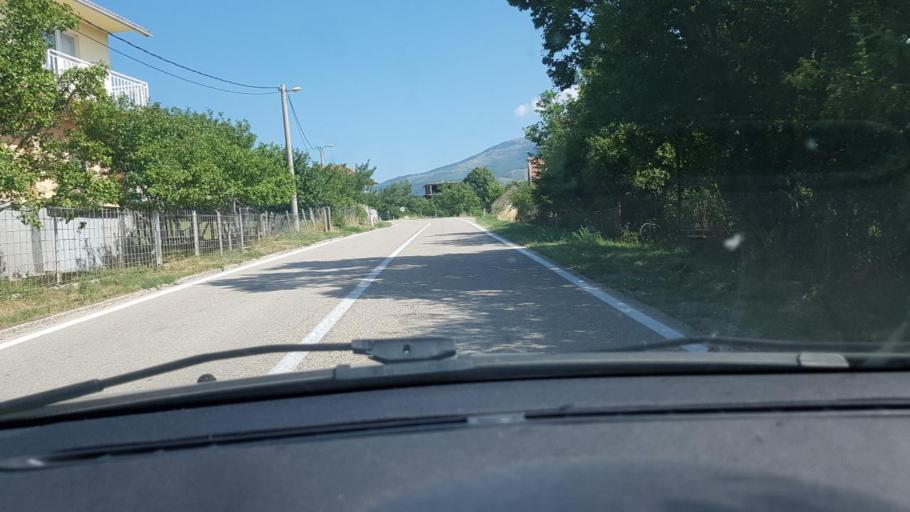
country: BA
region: Federation of Bosnia and Herzegovina
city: Bosansko Grahovo
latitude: 44.0779
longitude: 16.5711
